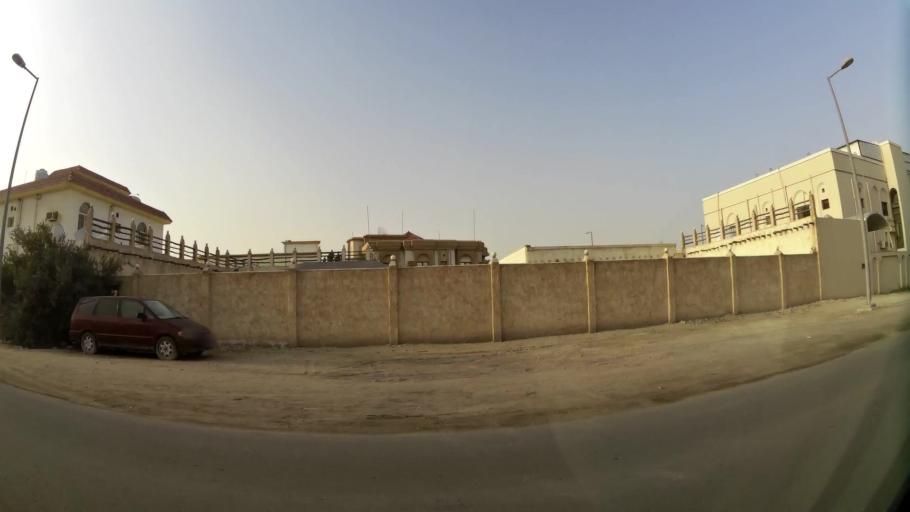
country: QA
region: Baladiyat ar Rayyan
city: Ar Rayyan
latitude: 25.2477
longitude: 51.4480
